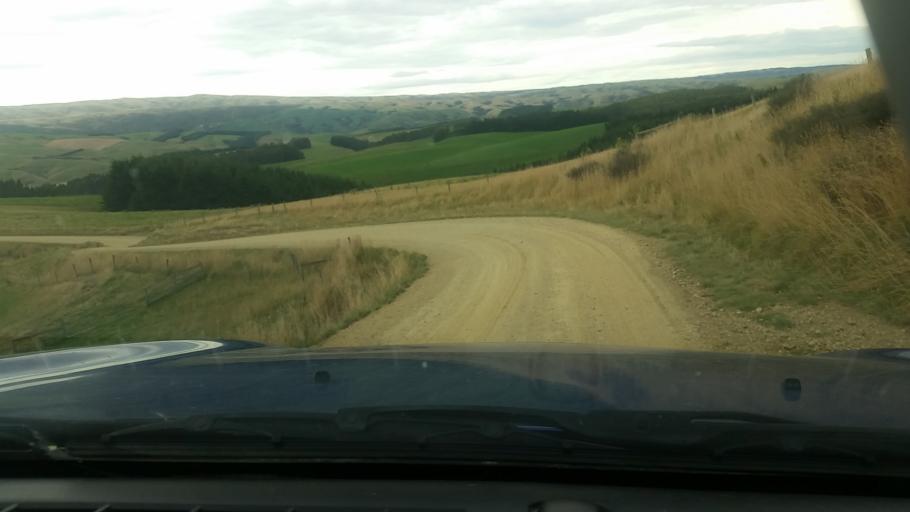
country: NZ
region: Otago
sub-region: Clutha District
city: Balclutha
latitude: -45.6827
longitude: 169.4926
